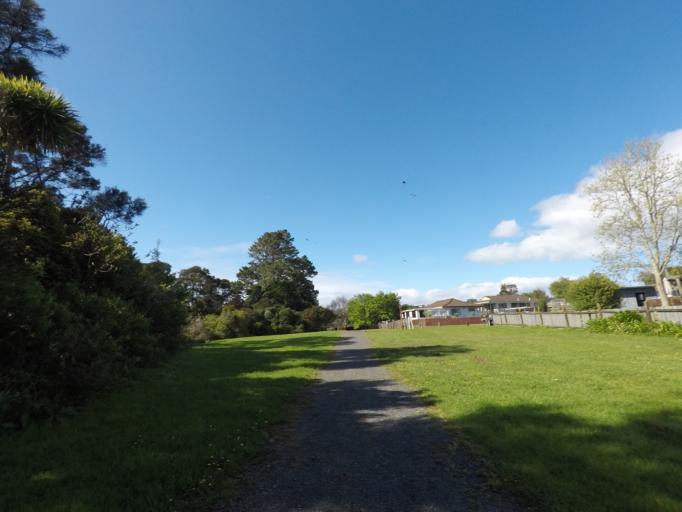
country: NZ
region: Auckland
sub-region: Auckland
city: Rosebank
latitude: -36.8566
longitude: 174.5995
